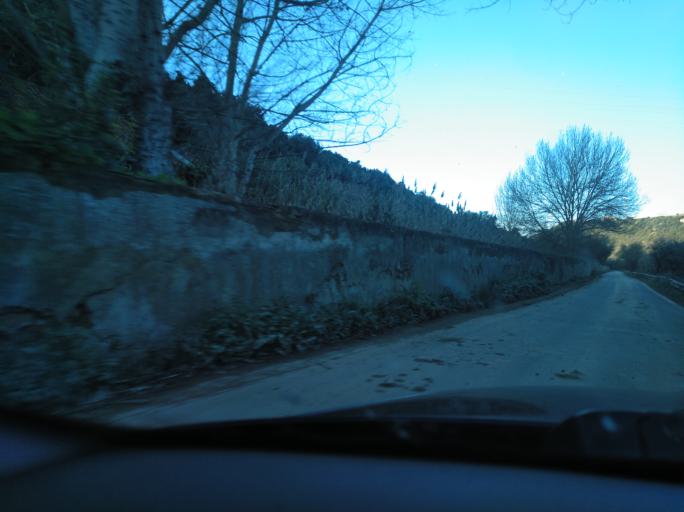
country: PT
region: Lisbon
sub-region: Loures
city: Bobadela
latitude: 38.8058
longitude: -9.1090
